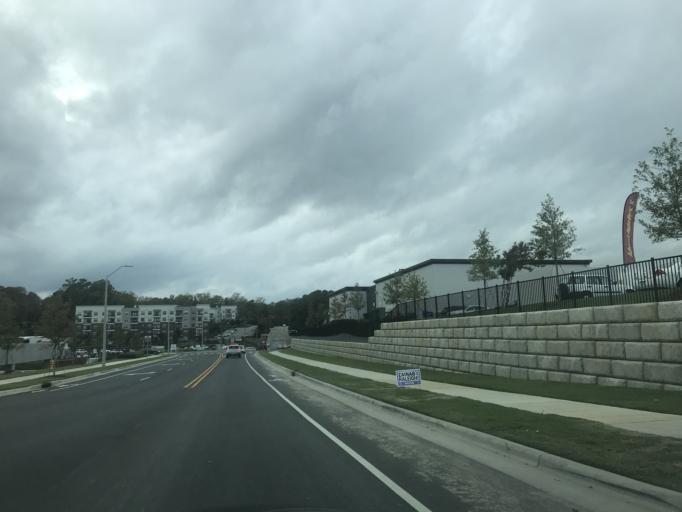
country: US
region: North Carolina
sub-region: Wake County
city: Raleigh
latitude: 35.8221
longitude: -78.6199
